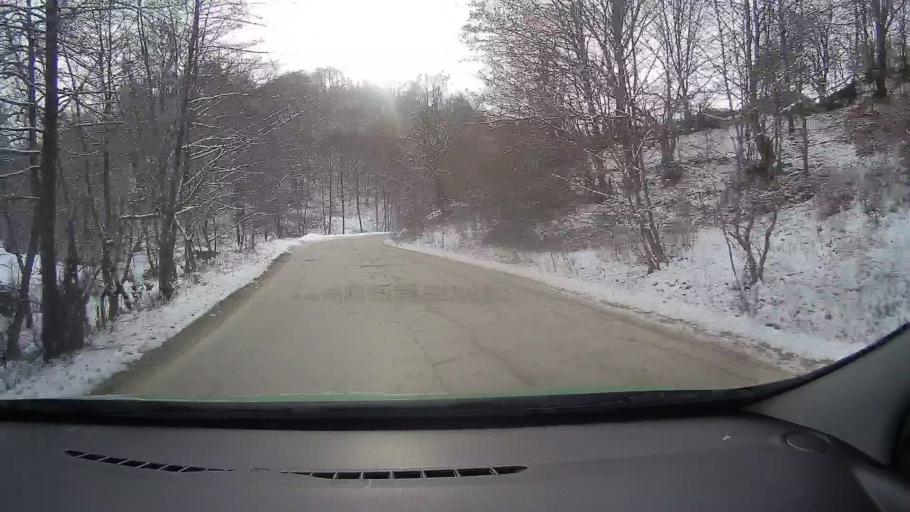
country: RO
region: Alba
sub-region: Oras Zlatna
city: Zlatna
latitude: 46.1082
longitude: 23.1960
